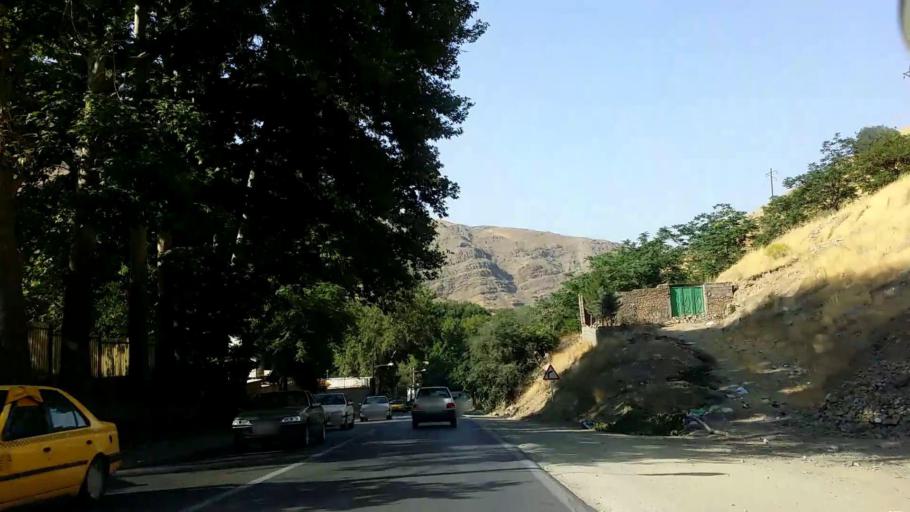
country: IR
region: Alborz
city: Karaj
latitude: 35.8425
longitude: 51.0572
